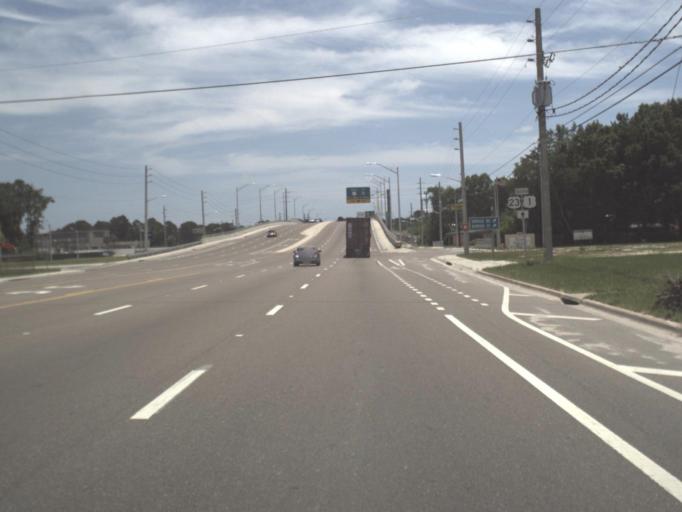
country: US
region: Florida
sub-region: Duval County
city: Jacksonville
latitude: 30.3632
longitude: -81.7176
